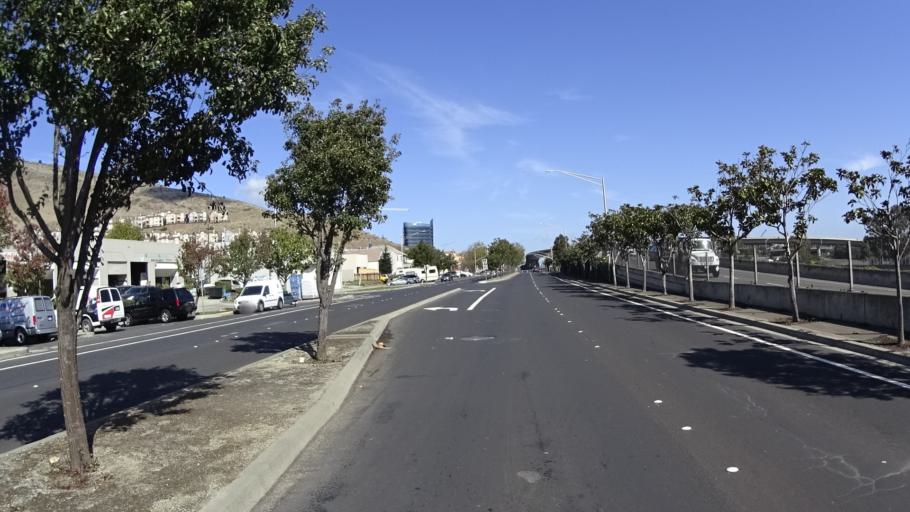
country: US
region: California
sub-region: San Mateo County
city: South San Francisco
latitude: 37.6618
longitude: -122.4028
